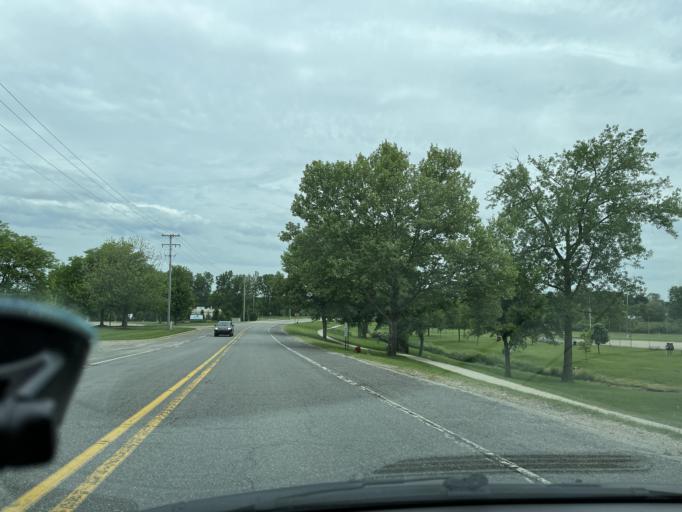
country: US
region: Michigan
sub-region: Barry County
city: Hastings
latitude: 42.6458
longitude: -85.3088
